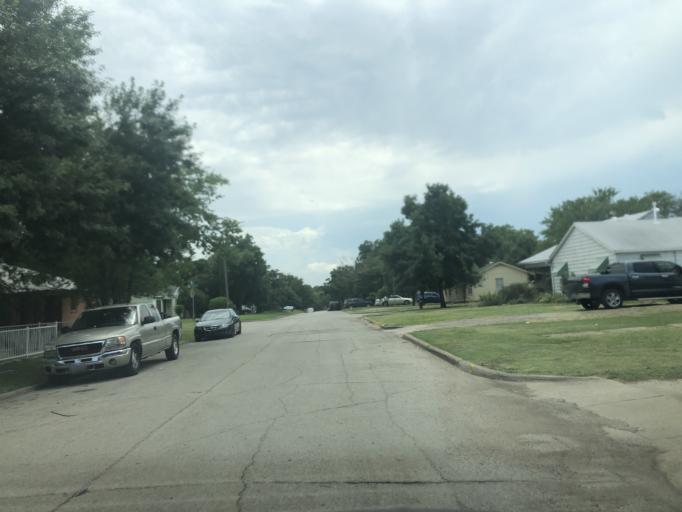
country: US
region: Texas
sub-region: Dallas County
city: Grand Prairie
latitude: 32.7393
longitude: -97.0013
